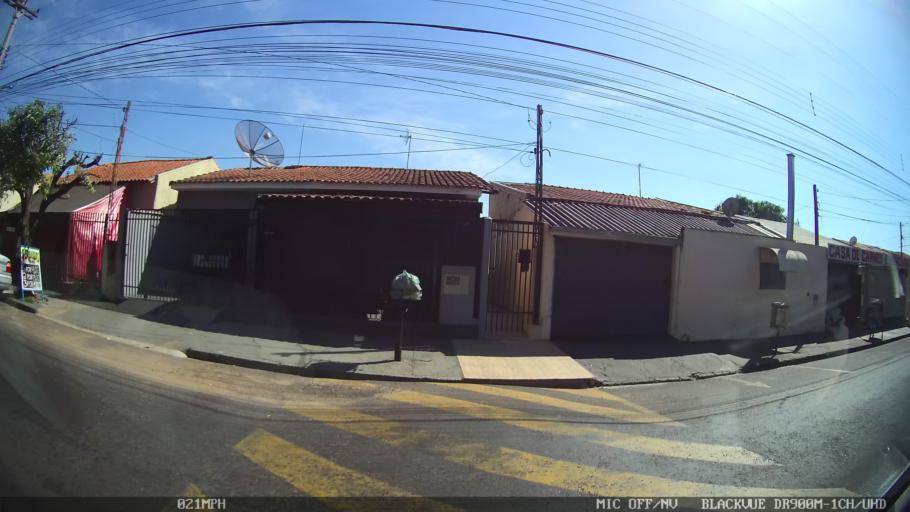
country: BR
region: Sao Paulo
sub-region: Sao Jose Do Rio Preto
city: Sao Jose do Rio Preto
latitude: -20.7753
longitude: -49.4185
